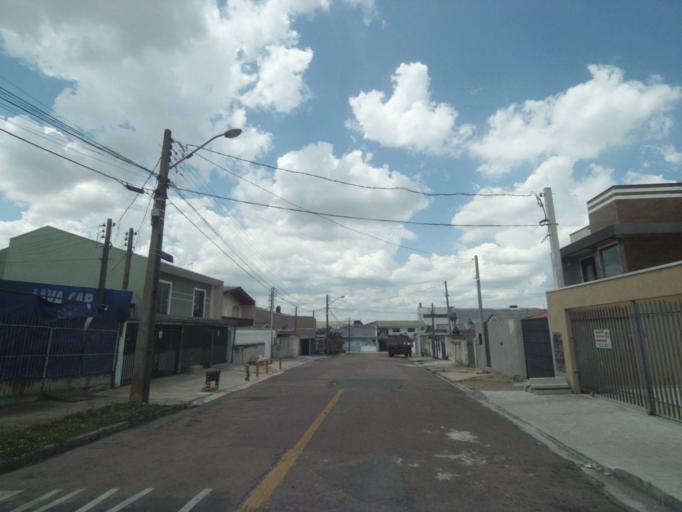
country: BR
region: Parana
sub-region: Sao Jose Dos Pinhais
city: Sao Jose dos Pinhais
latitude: -25.5395
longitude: -49.2714
